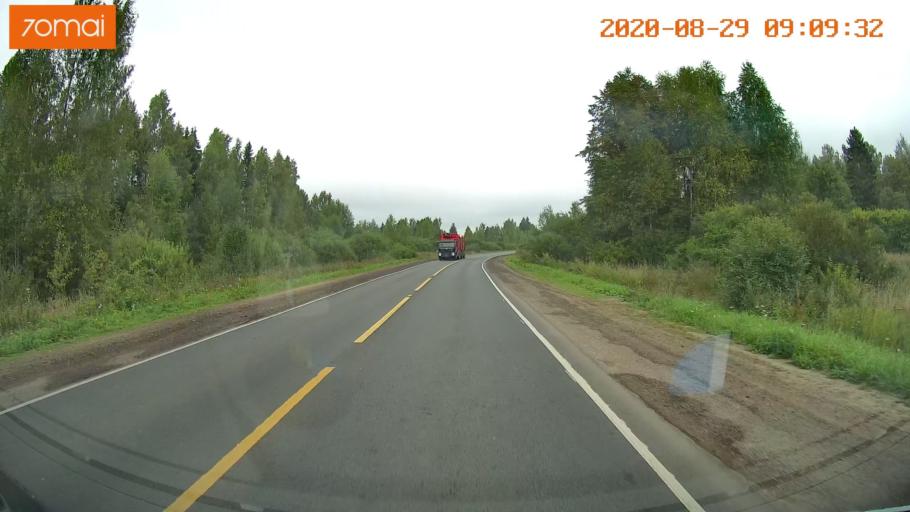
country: RU
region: Ivanovo
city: Kineshma
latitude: 57.4050
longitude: 42.0542
